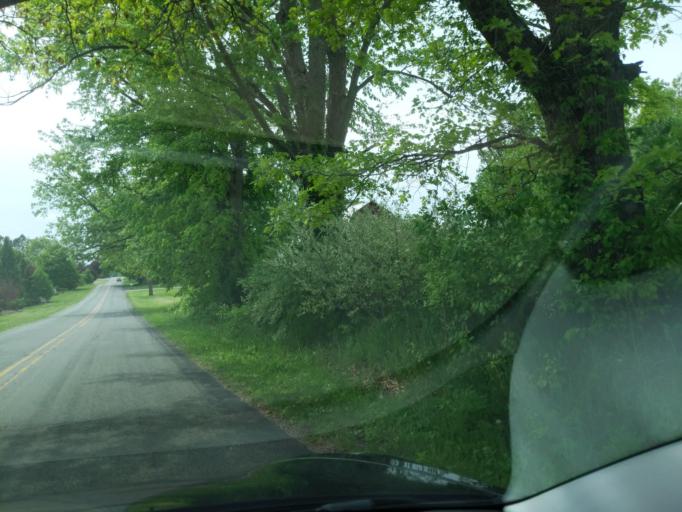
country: US
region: Michigan
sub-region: Ingham County
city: Leslie
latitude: 42.4247
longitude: -84.3081
